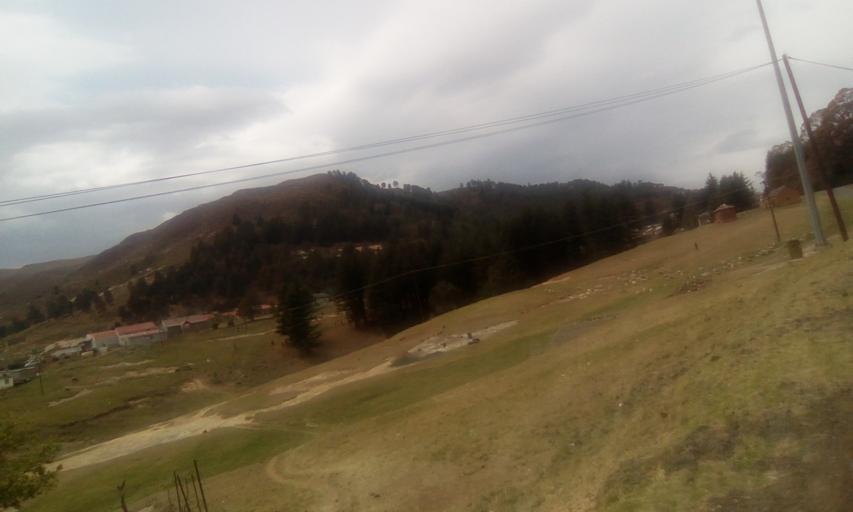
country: LS
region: Qacha's Nek
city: Qacha's Nek
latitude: -30.1194
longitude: 28.6890
